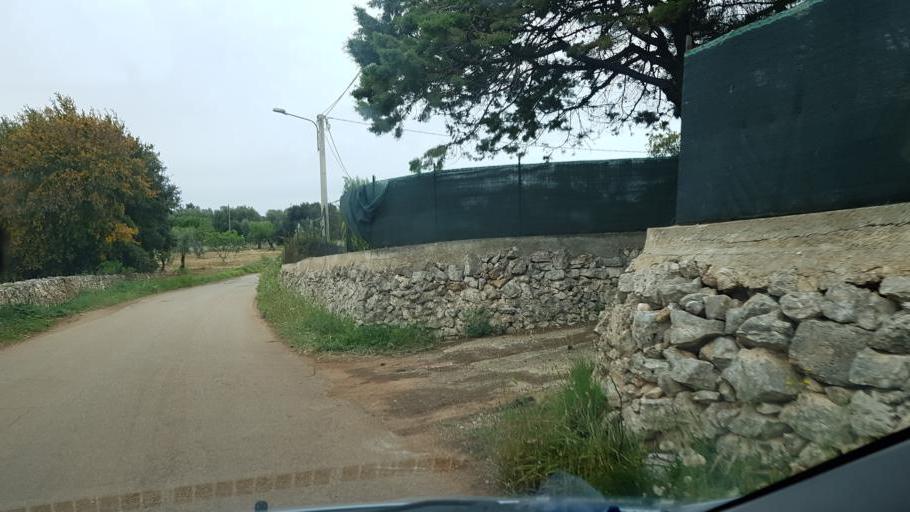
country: IT
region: Apulia
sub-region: Provincia di Brindisi
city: San Vito dei Normanni
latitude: 40.6651
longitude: 17.7428
